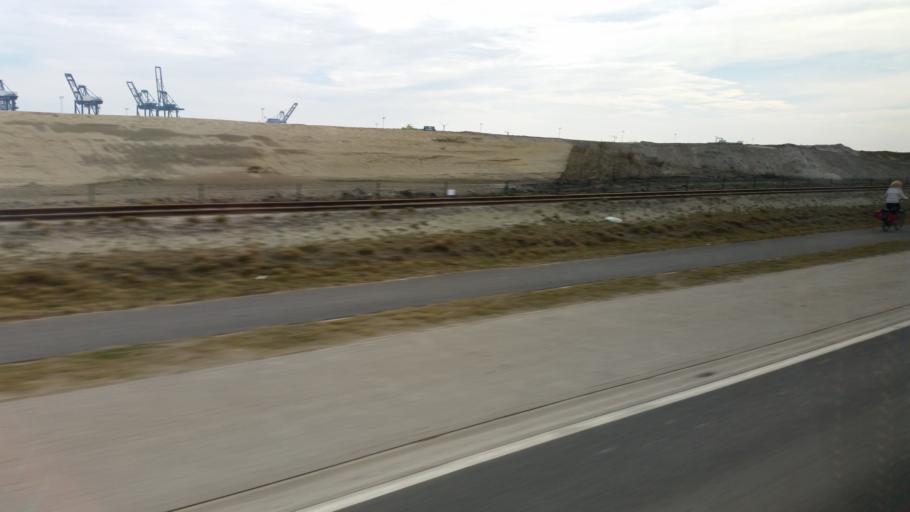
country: BE
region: Flanders
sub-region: Provincie Oost-Vlaanderen
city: Beveren
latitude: 51.3004
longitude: 4.2459
